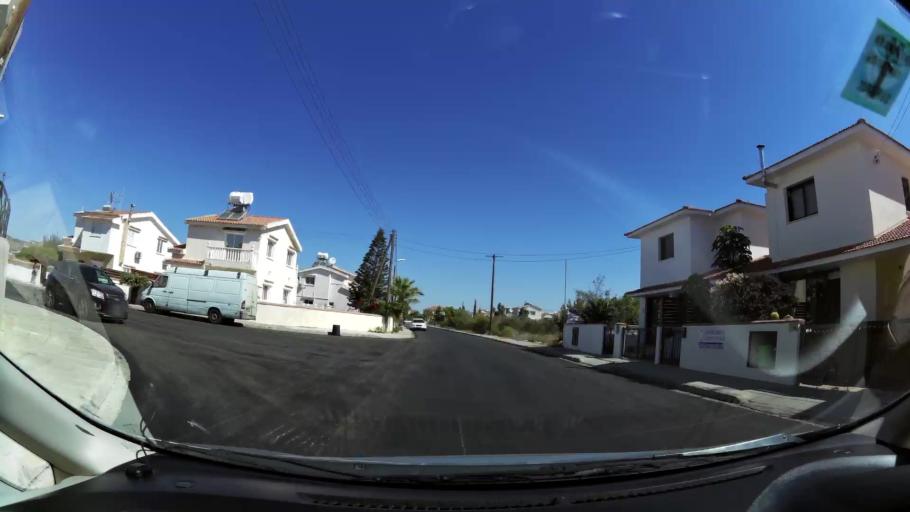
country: CY
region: Larnaka
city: Voroklini
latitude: 34.9614
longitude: 33.6537
